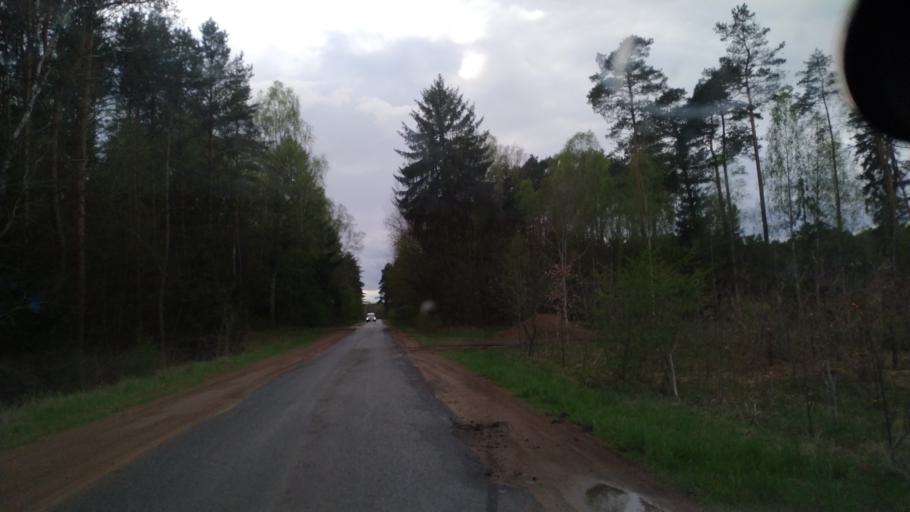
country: PL
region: Pomeranian Voivodeship
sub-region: Powiat starogardzki
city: Osiek
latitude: 53.6915
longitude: 18.5291
